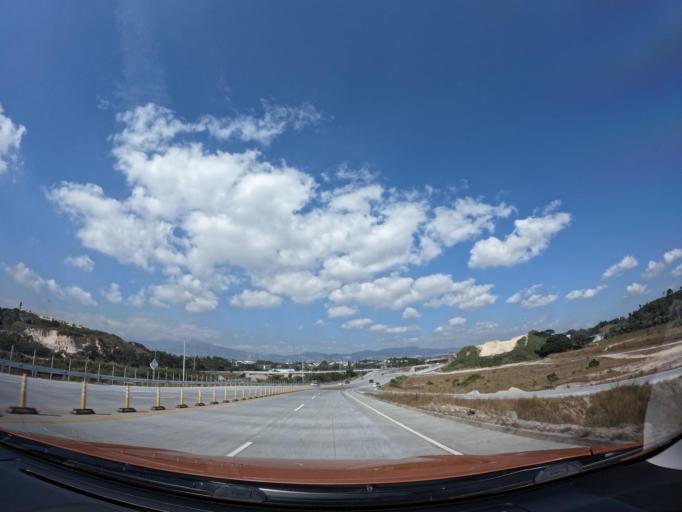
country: GT
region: Guatemala
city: Petapa
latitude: 14.4972
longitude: -90.5423
